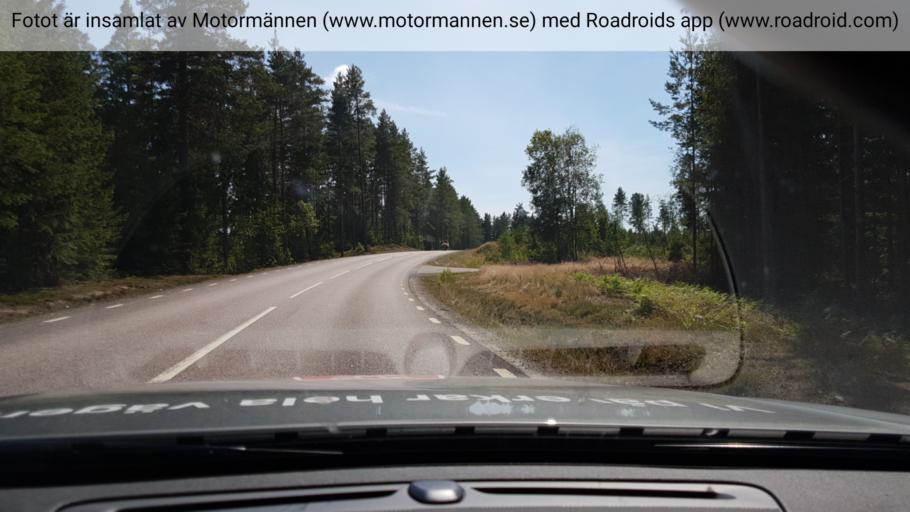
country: SE
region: OErebro
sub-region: Laxa Kommun
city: Laxa
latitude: 58.9276
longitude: 14.6555
